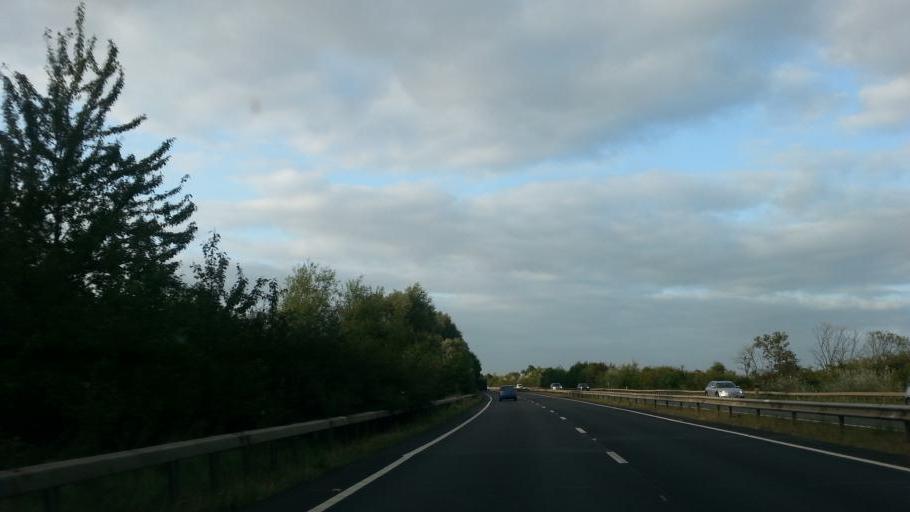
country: GB
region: England
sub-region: Oxfordshire
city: Kidlington
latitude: 51.8158
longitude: -1.2650
